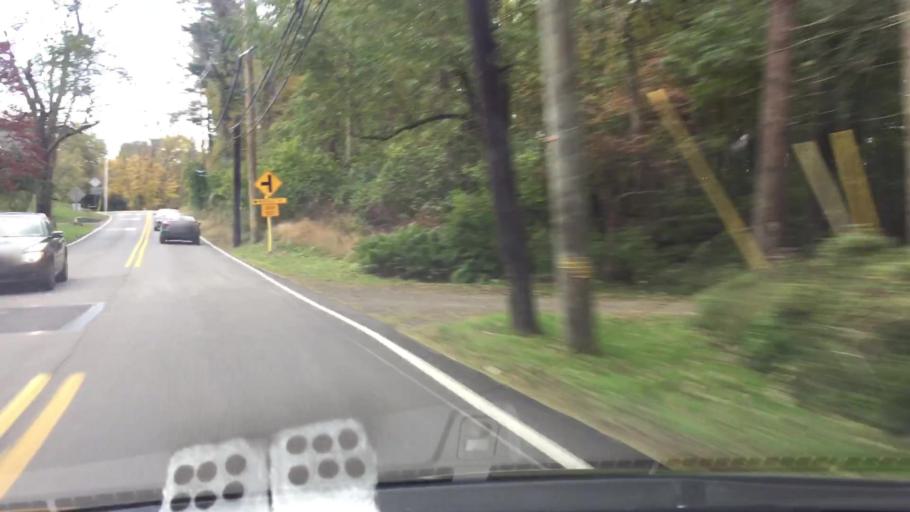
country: US
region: Pennsylvania
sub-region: Delaware County
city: Media
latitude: 39.9219
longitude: -75.4062
